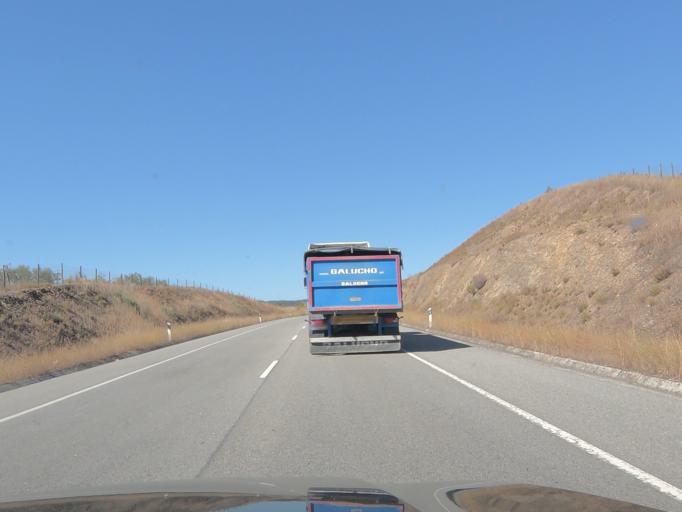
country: PT
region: Vila Real
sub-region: Valpacos
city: Valpacos
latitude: 41.5436
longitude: -7.2565
